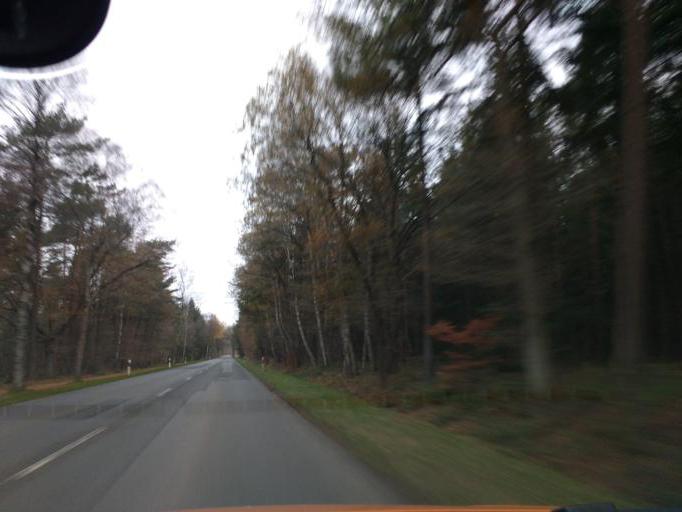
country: DE
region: Lower Saxony
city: Hatten
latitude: 53.0747
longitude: 8.4133
